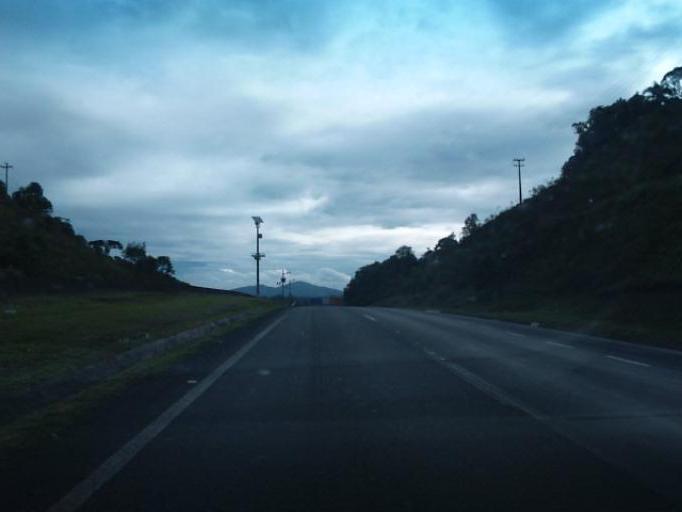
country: BR
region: Parana
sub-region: Campina Grande Do Sul
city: Campina Grande do Sul
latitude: -25.2706
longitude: -48.9196
